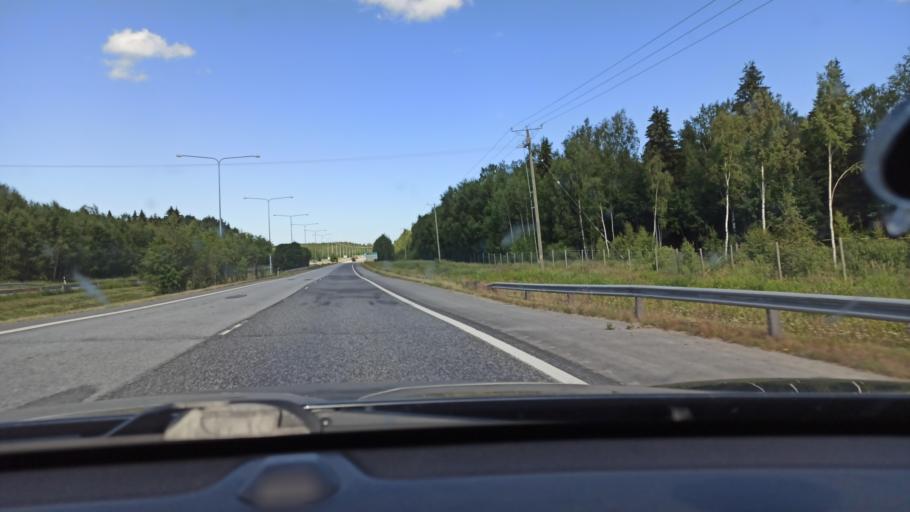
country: FI
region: Ostrobothnia
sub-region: Vaasa
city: Ristinummi
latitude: 63.0407
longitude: 21.7316
